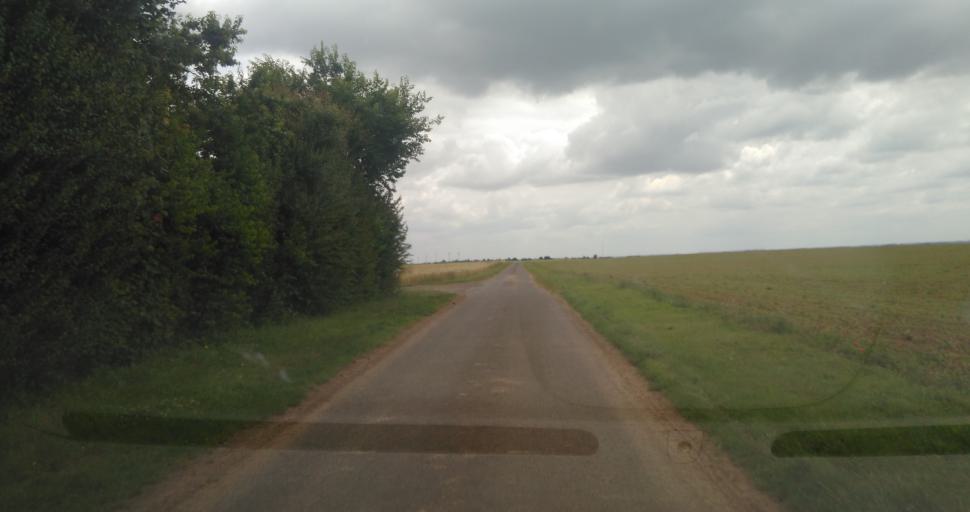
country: FR
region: Pays de la Loire
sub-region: Departement de la Vendee
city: Sainte-Gemme-la-Plaine
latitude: 46.5160
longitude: -1.0859
